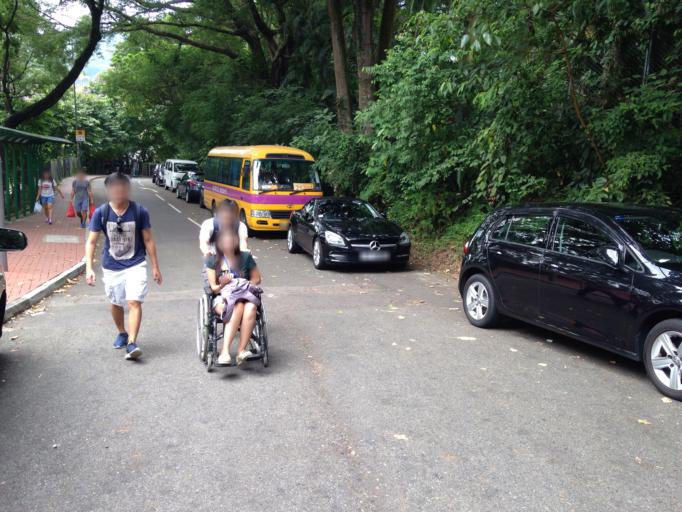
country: HK
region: Tai Po
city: Tai Po
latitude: 22.4462
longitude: 114.1699
